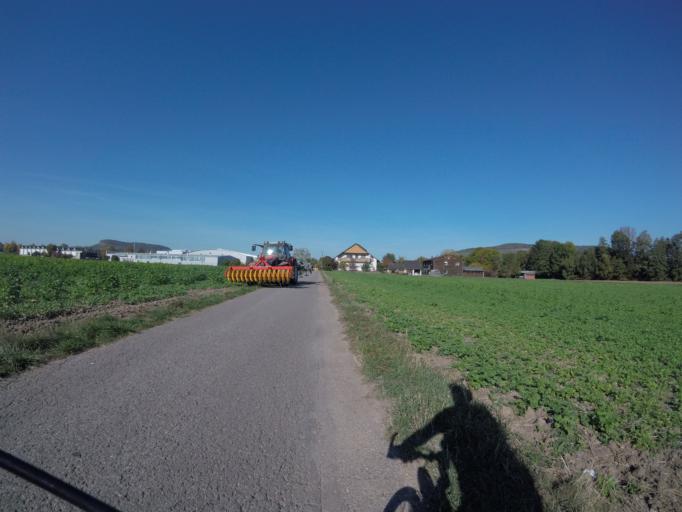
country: DE
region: Baden-Wuerttemberg
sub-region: Regierungsbezirk Stuttgart
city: Sersheim
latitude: 48.9749
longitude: 8.9954
